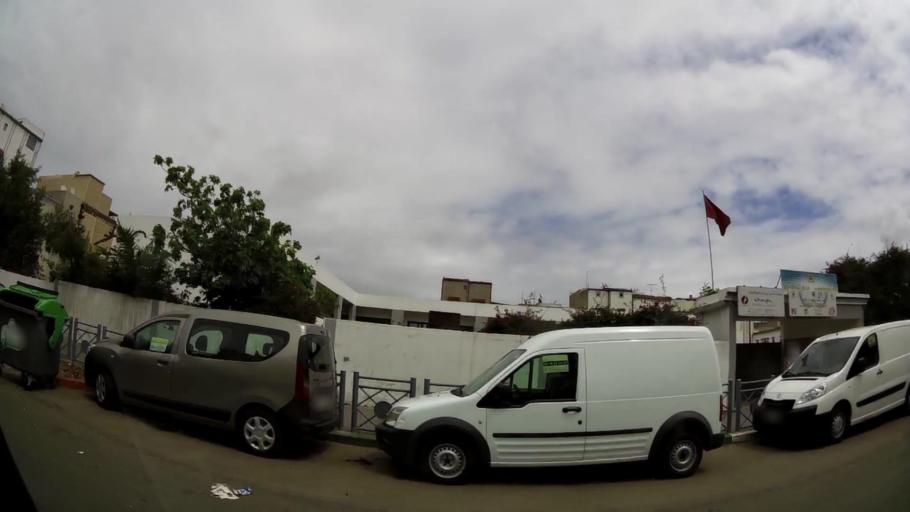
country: MA
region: Grand Casablanca
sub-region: Mediouna
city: Tit Mellil
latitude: 33.6130
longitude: -7.5025
